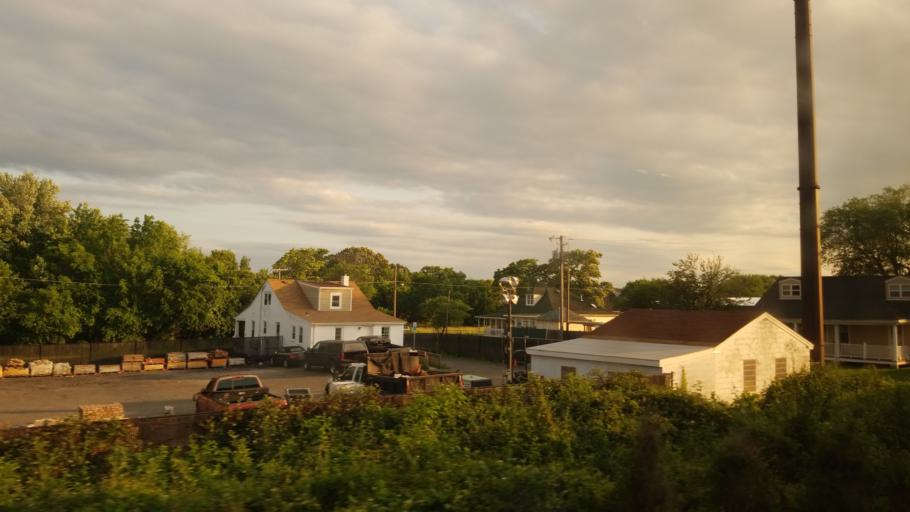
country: US
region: Virginia
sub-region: City of Manassas
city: Manassas
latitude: 38.7491
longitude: -77.4824
